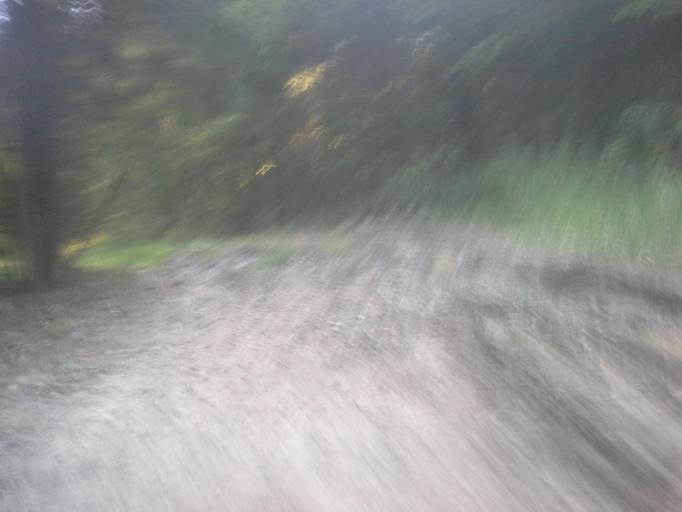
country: RU
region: Moskovskaya
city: Selyatino
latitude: 55.4612
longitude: 36.9867
